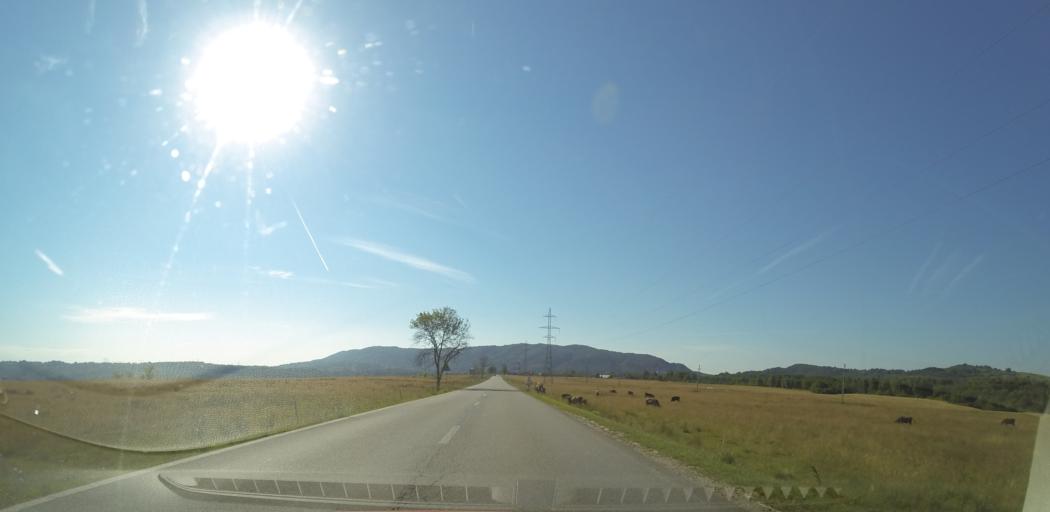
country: RO
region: Valcea
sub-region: Comuna Slatioara
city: Slatioara
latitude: 45.1284
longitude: 23.8705
